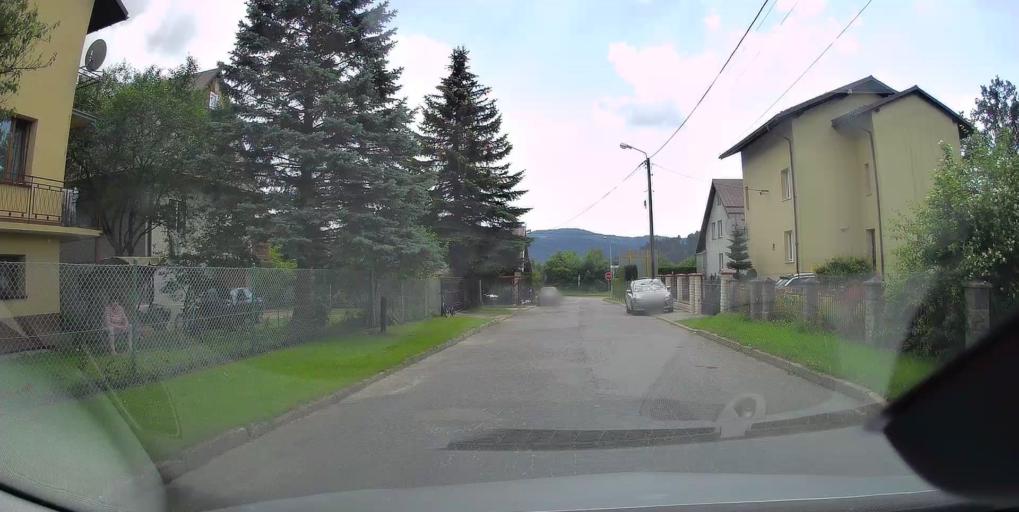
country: PL
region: Lesser Poland Voivodeship
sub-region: Powiat nowosadecki
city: Krynica-Zdroj
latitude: 49.3855
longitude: 20.9528
